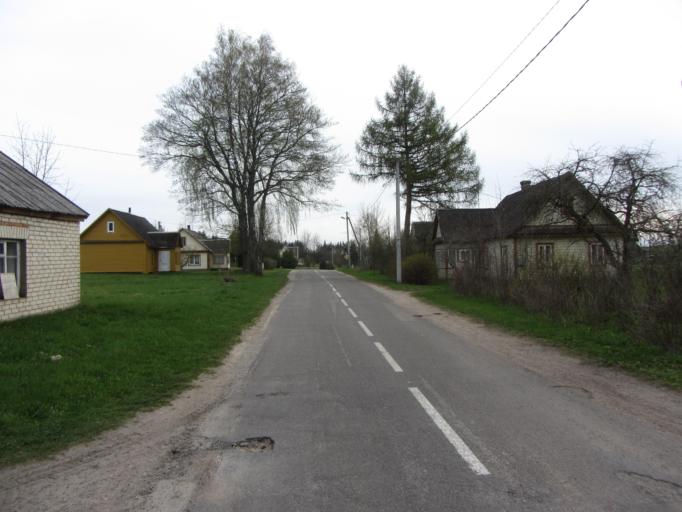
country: LT
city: Zarasai
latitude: 55.5773
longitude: 26.1332
